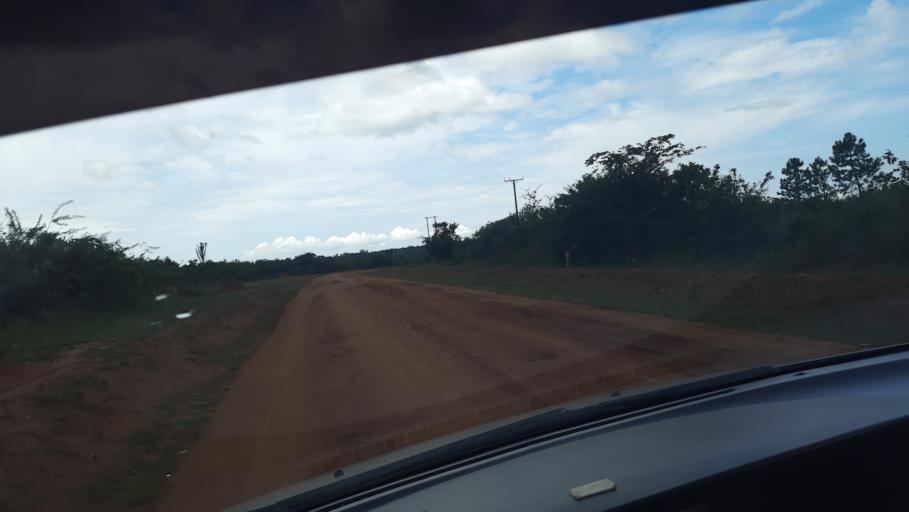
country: UG
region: Central Region
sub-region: Nakasongola District
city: Nakasongola
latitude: 1.3736
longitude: 32.4840
